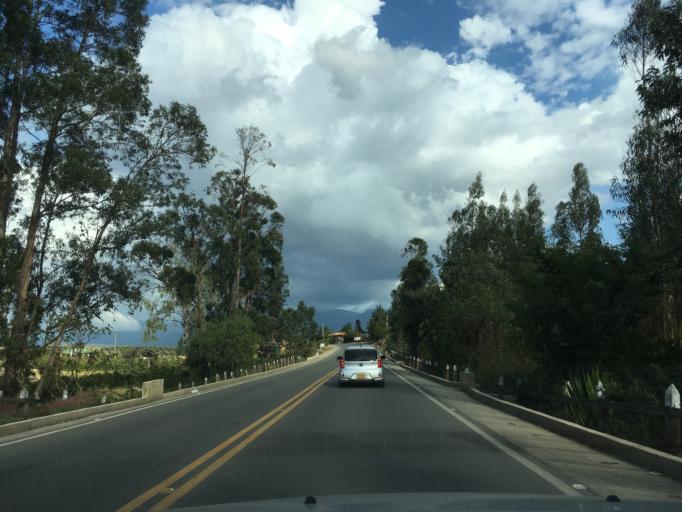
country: CO
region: Boyaca
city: Sutamarchan
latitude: 5.6206
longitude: -73.6061
